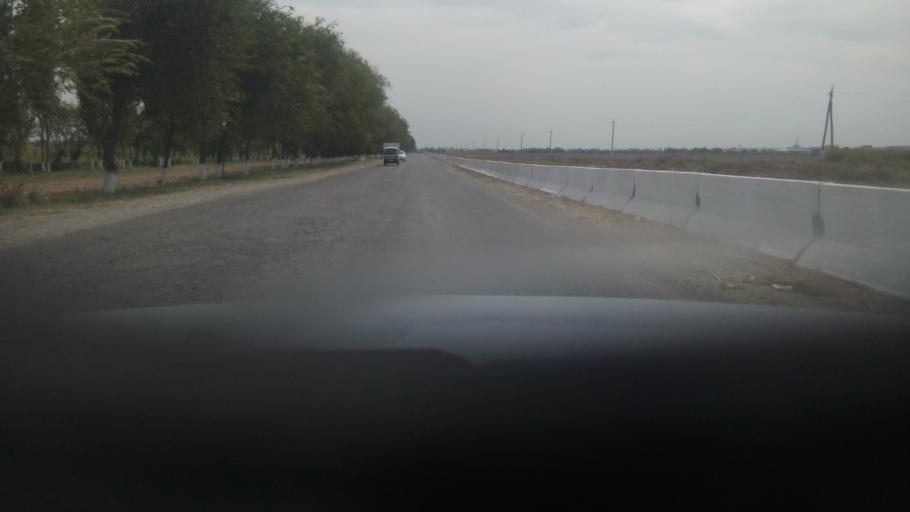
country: UZ
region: Sirdaryo
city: Guliston
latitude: 40.5146
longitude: 68.7942
